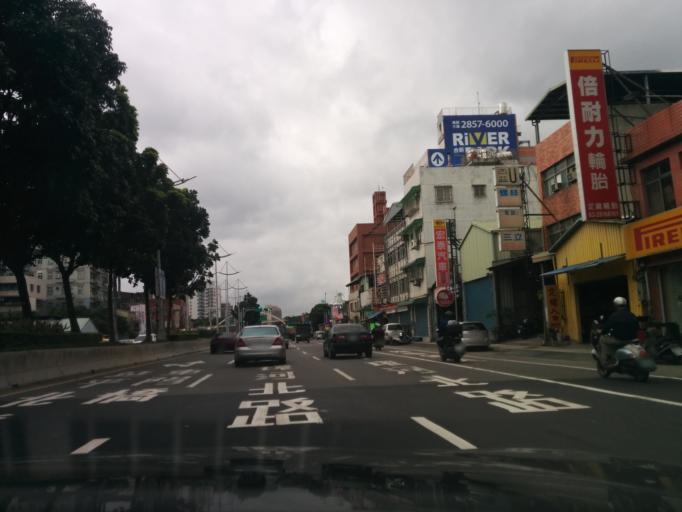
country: TW
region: Taipei
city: Taipei
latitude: 25.0922
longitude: 121.4994
